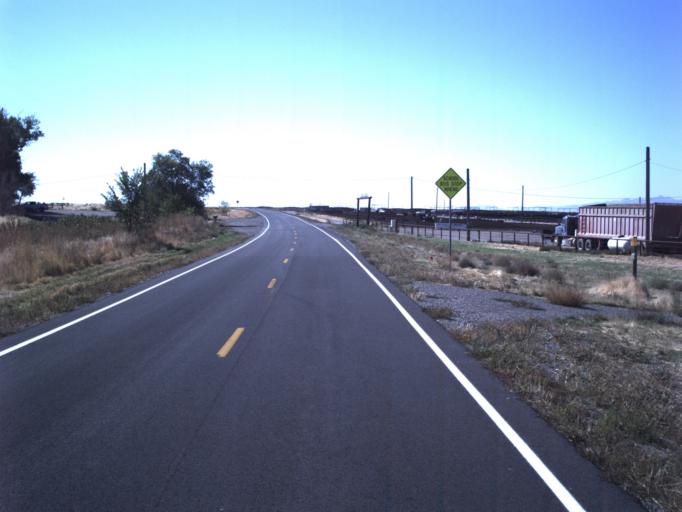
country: US
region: Utah
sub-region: Tooele County
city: Grantsville
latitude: 40.5382
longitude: -112.7465
